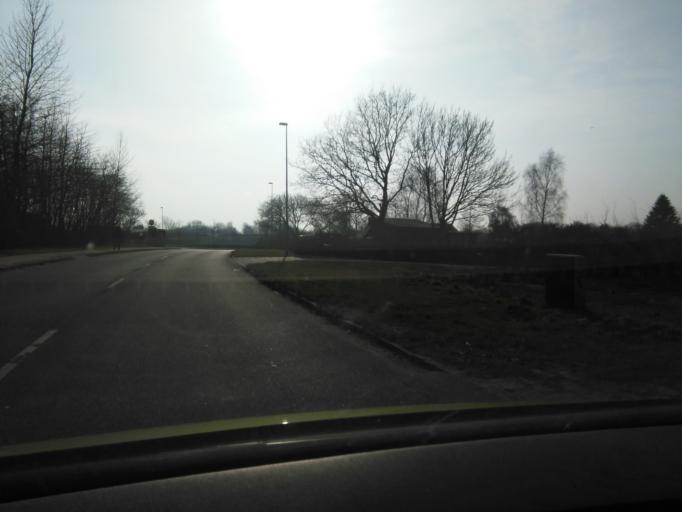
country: DK
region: Central Jutland
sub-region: Arhus Kommune
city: Marslet
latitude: 56.1053
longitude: 10.1661
